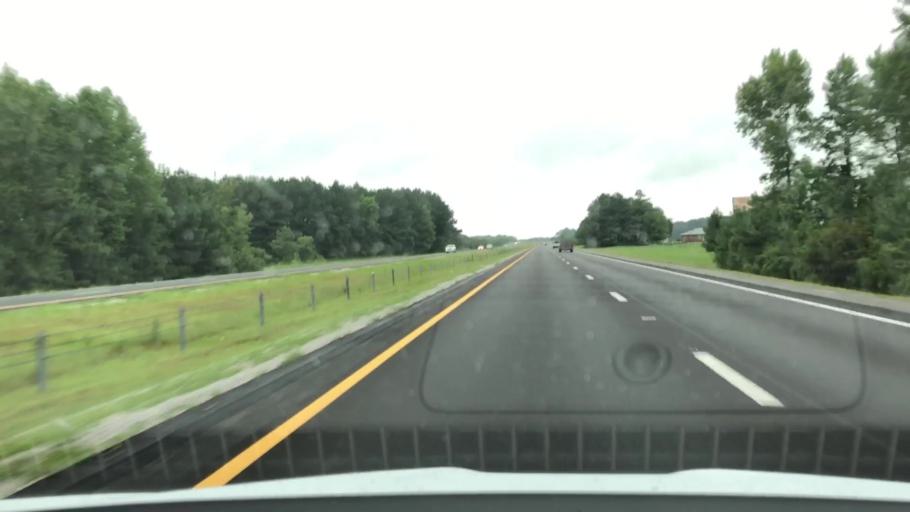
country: US
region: North Carolina
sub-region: Wayne County
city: Goldsboro
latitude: 35.4605
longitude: -77.9854
